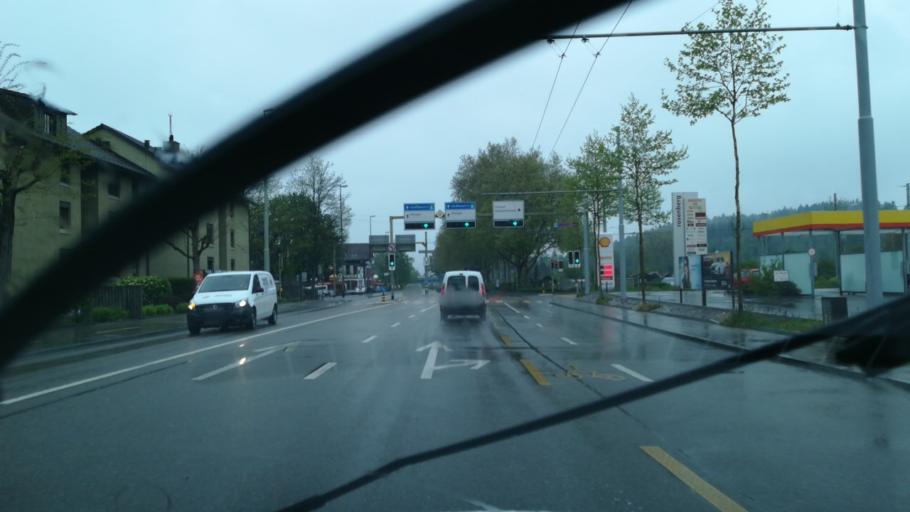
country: CH
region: Zurich
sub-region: Bezirk Winterthur
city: Veltheim
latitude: 47.5186
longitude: 8.7190
